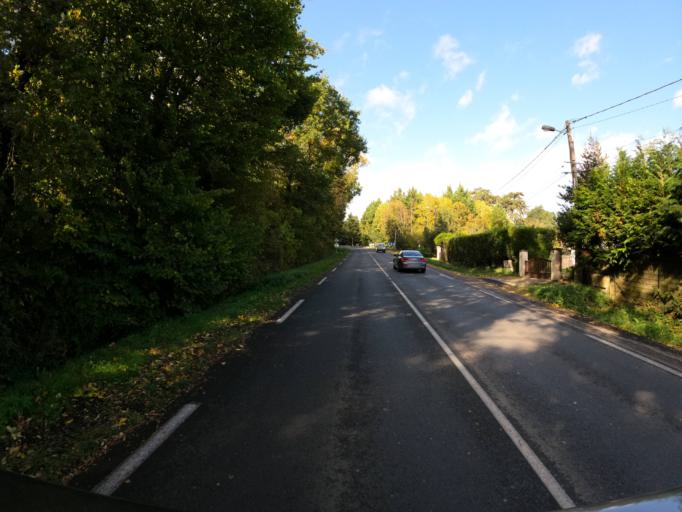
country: FR
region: Ile-de-France
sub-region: Departement de Seine-et-Marne
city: Montry
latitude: 48.8822
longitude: 2.8224
